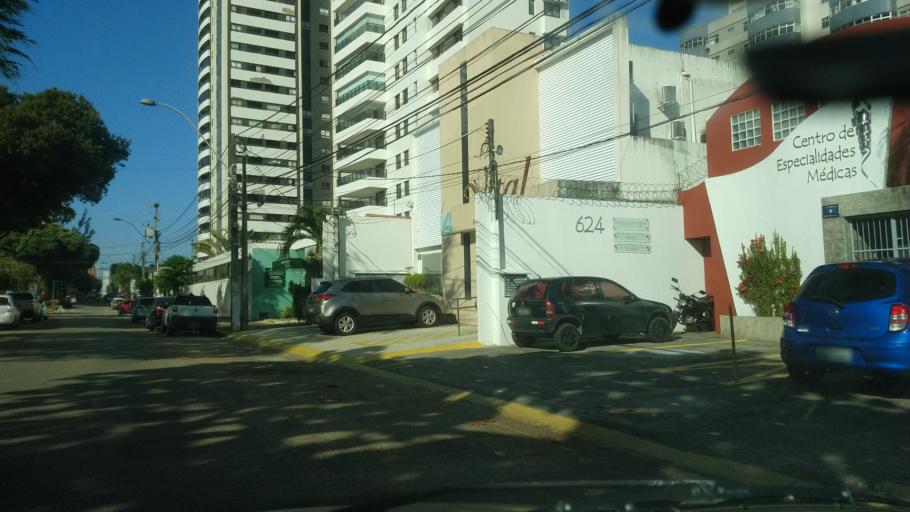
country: BR
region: Rio Grande do Norte
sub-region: Natal
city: Natal
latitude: -5.7881
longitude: -35.2001
